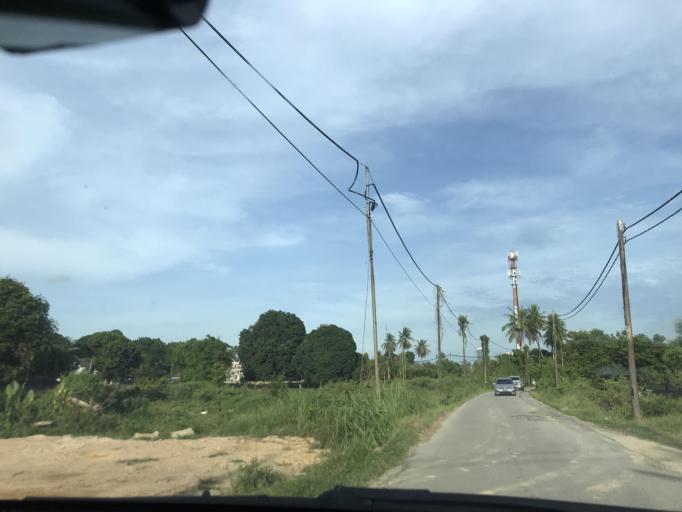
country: MY
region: Kelantan
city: Kota Bharu
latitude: 6.1282
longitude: 102.2211
